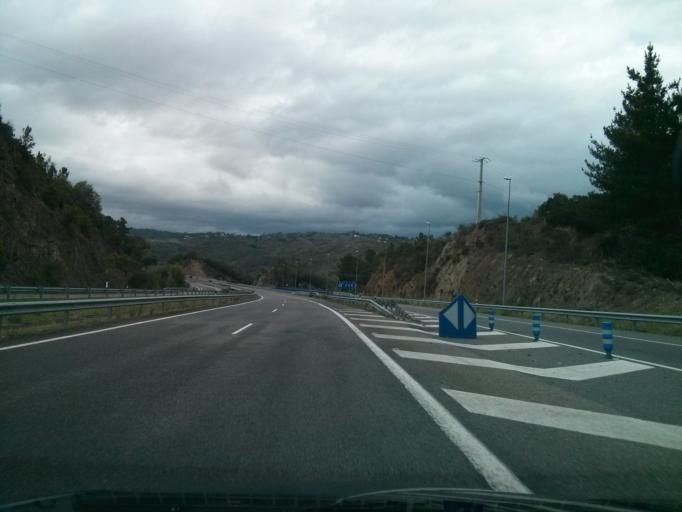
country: ES
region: Galicia
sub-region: Provincia de Ourense
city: Ourense
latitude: 42.3410
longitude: -7.8849
